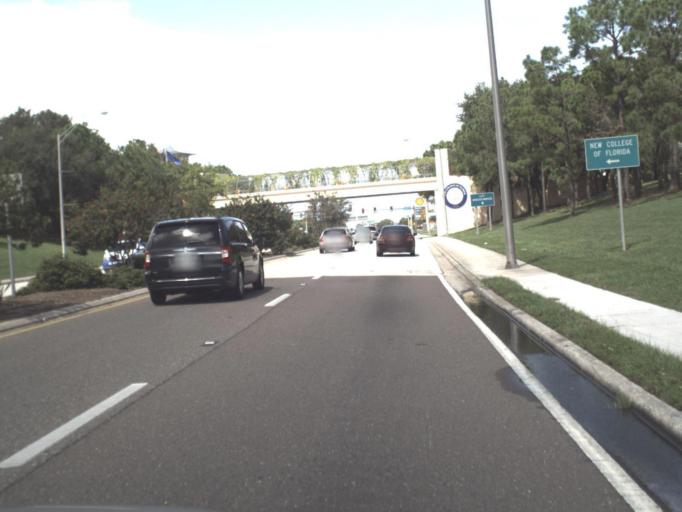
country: US
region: Florida
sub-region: Manatee County
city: Whitfield
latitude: 27.3843
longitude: -82.5575
